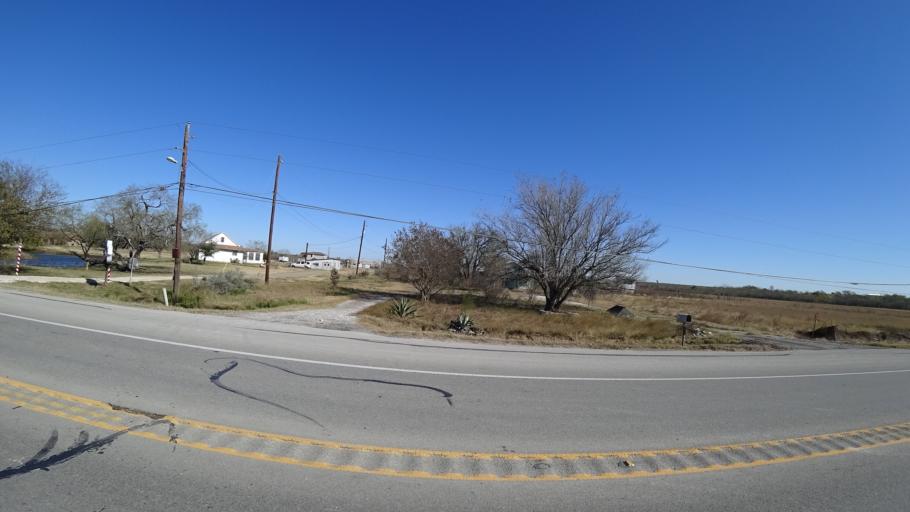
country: US
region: Texas
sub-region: Travis County
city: Garfield
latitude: 30.1151
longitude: -97.6288
